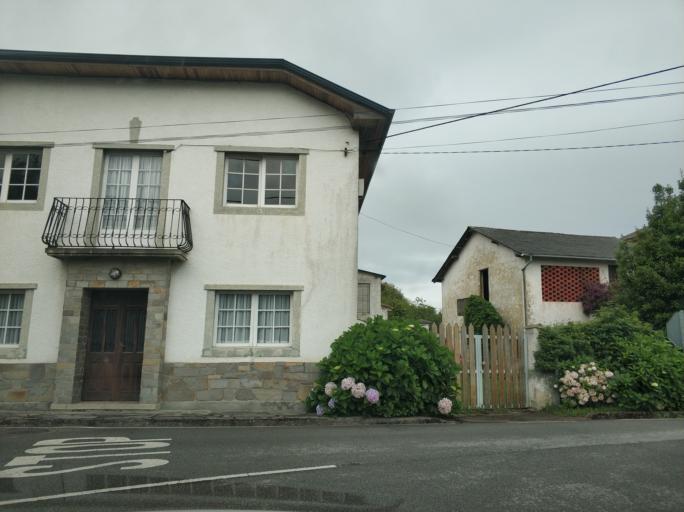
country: ES
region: Asturias
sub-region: Province of Asturias
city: Salas
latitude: 43.5461
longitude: -6.3867
